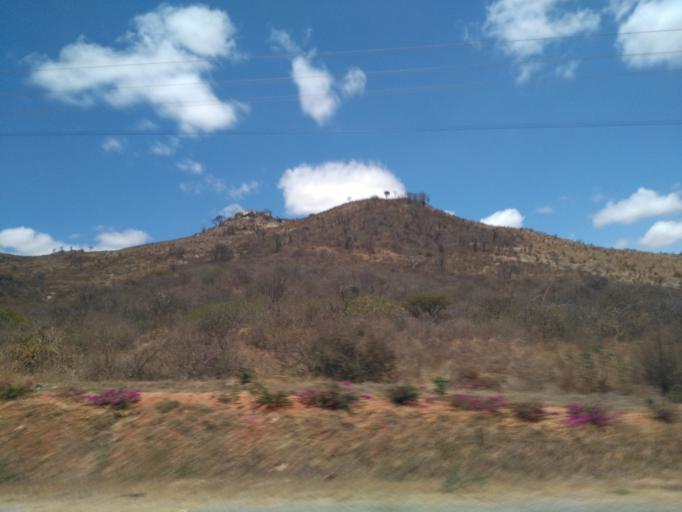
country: TZ
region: Dodoma
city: Kisasa
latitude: -6.2212
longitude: 35.7837
